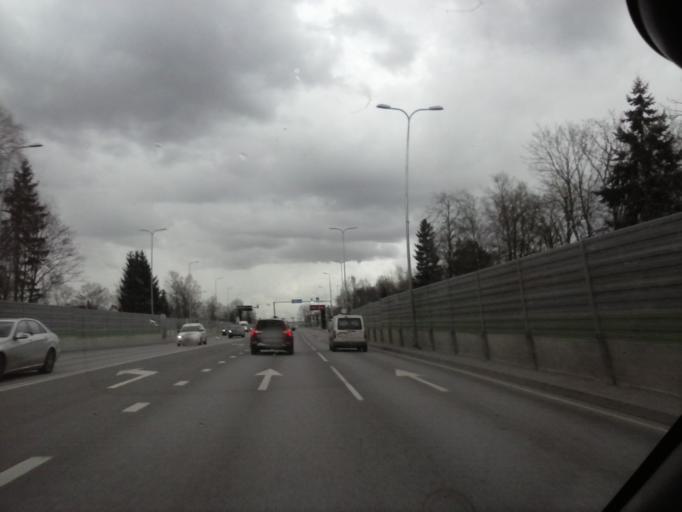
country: EE
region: Harju
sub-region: Tallinna linn
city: Tallinn
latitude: 59.4058
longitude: 24.8090
